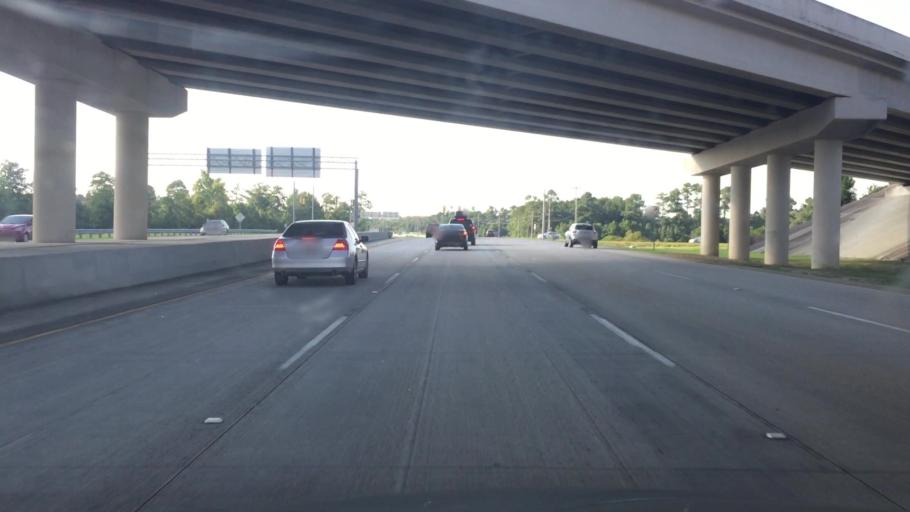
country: US
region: South Carolina
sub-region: Horry County
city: North Myrtle Beach
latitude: 33.8442
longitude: -78.7013
